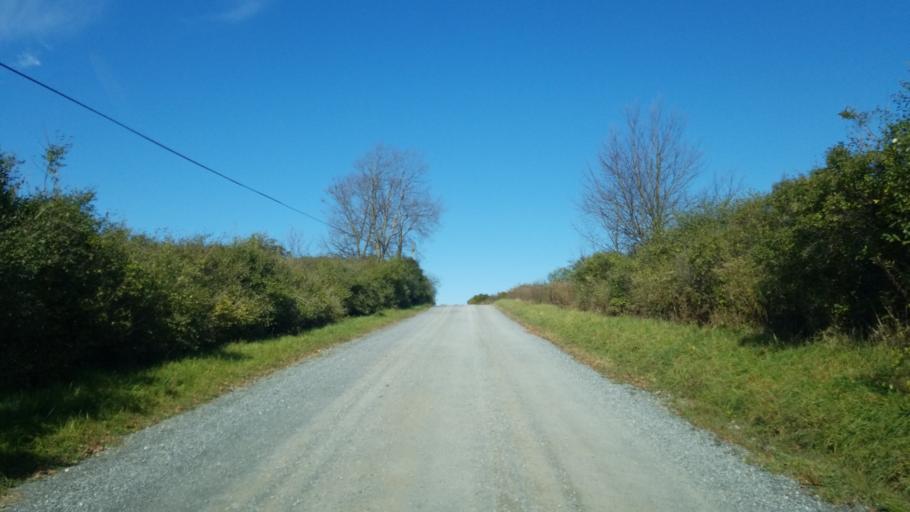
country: US
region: Pennsylvania
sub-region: Jefferson County
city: Falls Creek
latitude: 41.1825
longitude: -78.7830
